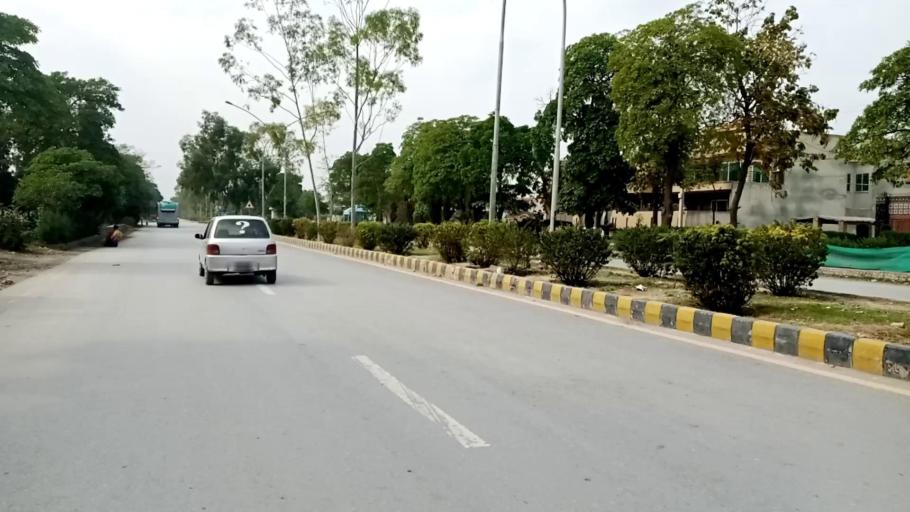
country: PK
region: Khyber Pakhtunkhwa
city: Peshawar
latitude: 33.9563
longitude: 71.4405
